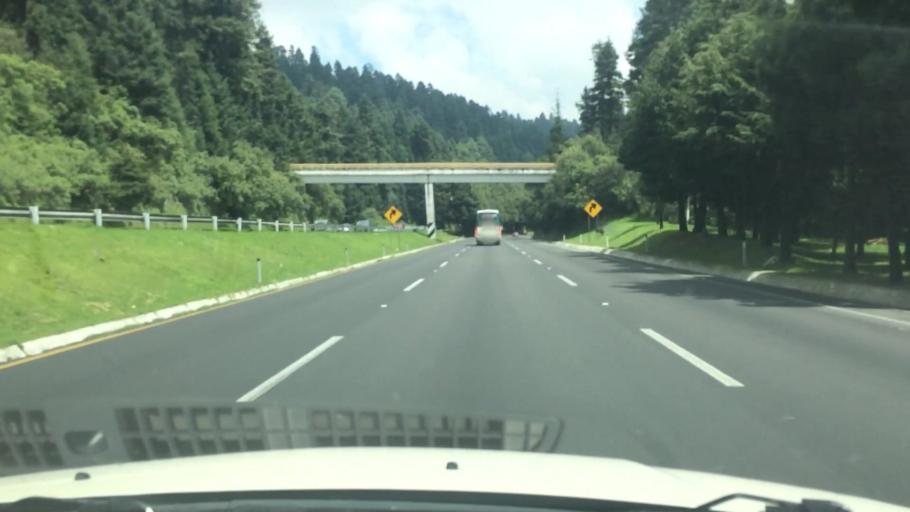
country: MX
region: Mexico City
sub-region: Cuajimalpa de Morelos
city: San Lorenzo Acopilco
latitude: 19.3024
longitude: -99.3469
